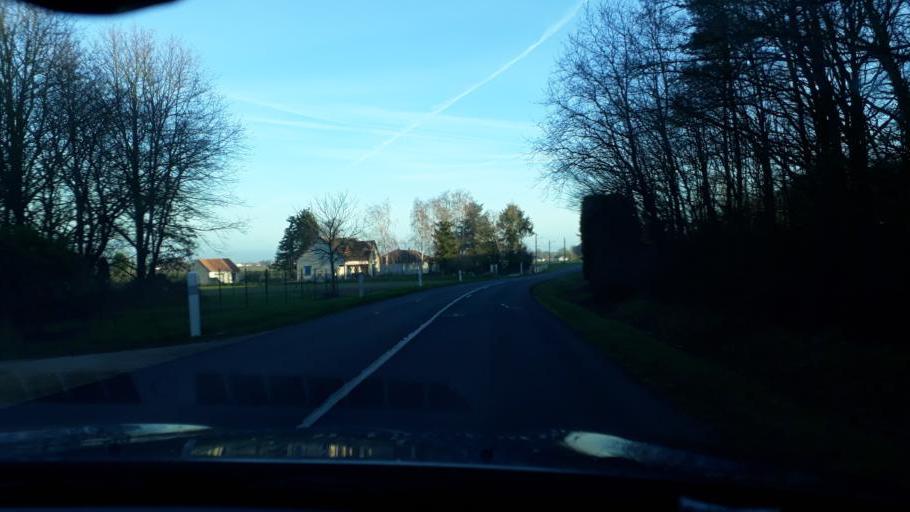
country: FR
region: Centre
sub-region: Departement du Loiret
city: Neuville-aux-Bois
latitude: 48.0459
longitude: 2.0499
